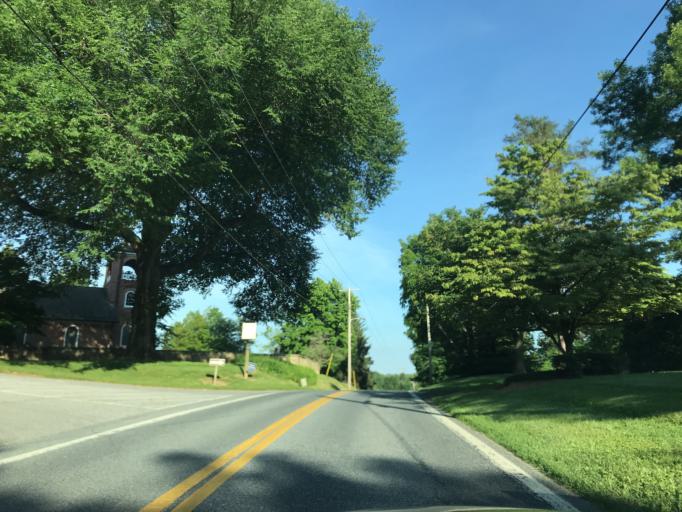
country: US
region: Maryland
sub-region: Baltimore County
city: Hunt Valley
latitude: 39.5613
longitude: -76.5705
